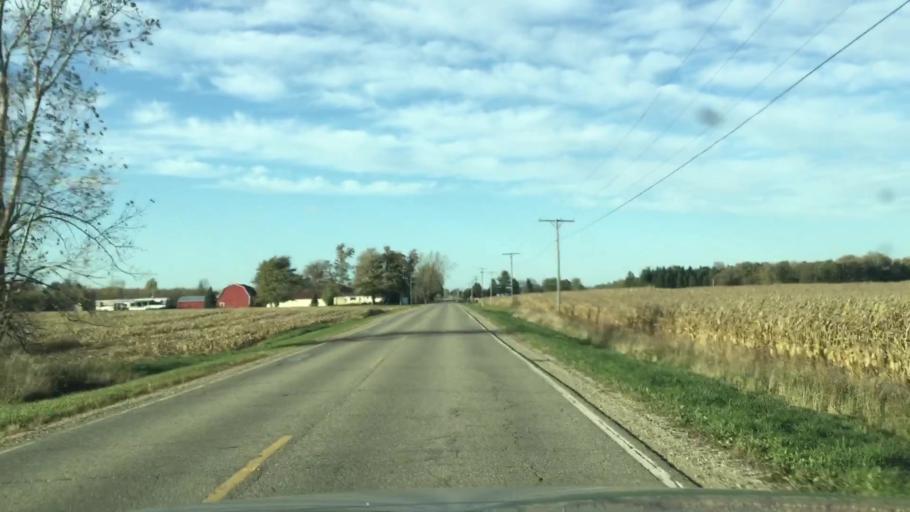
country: US
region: Michigan
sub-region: Lapeer County
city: North Branch
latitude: 43.2852
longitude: -83.1985
